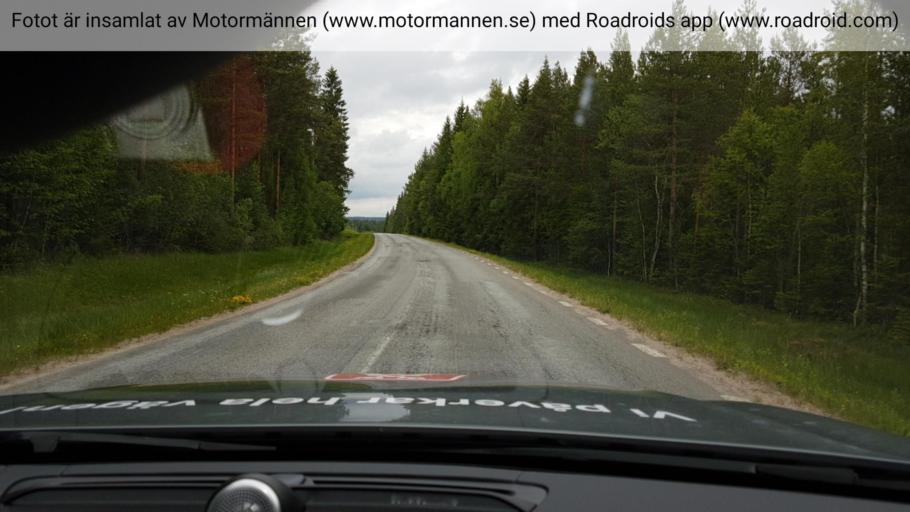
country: SE
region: Jaemtland
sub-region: Braecke Kommun
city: Braecke
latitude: 62.8767
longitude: 15.6028
